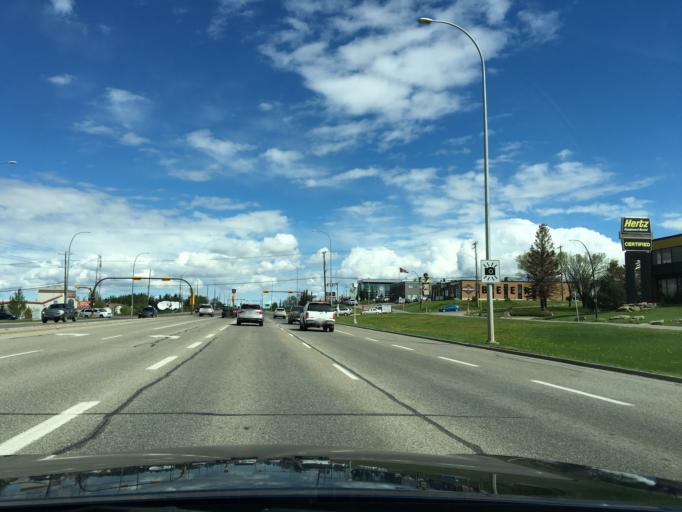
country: CA
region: Alberta
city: Calgary
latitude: 51.0513
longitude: -114.0016
